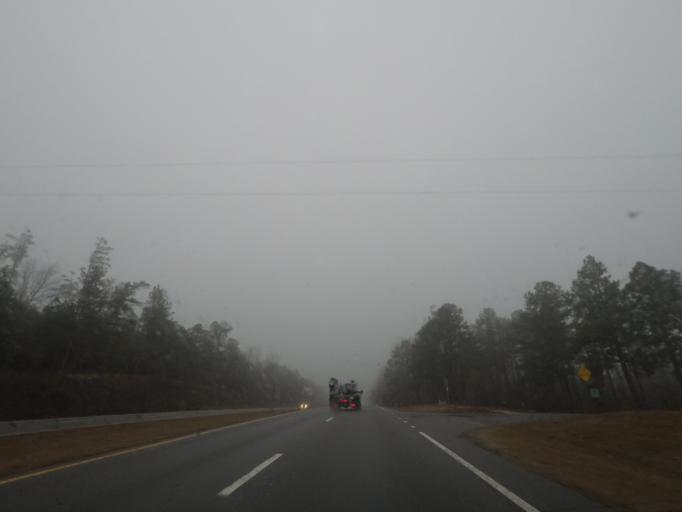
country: US
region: North Carolina
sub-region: Lee County
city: Sanford
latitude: 35.3968
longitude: -79.2314
